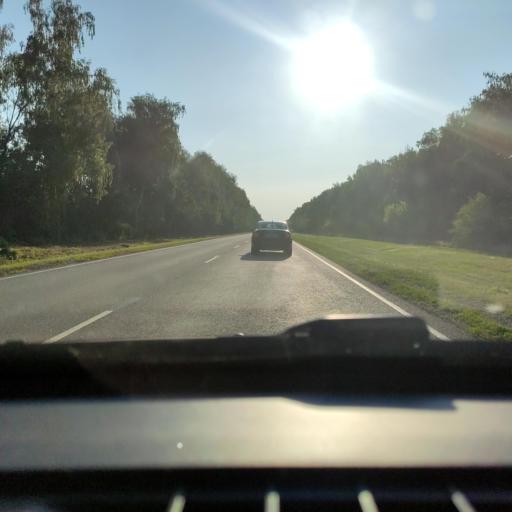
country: RU
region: Voronezj
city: Kashirskoye
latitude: 51.4603
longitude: 39.7510
